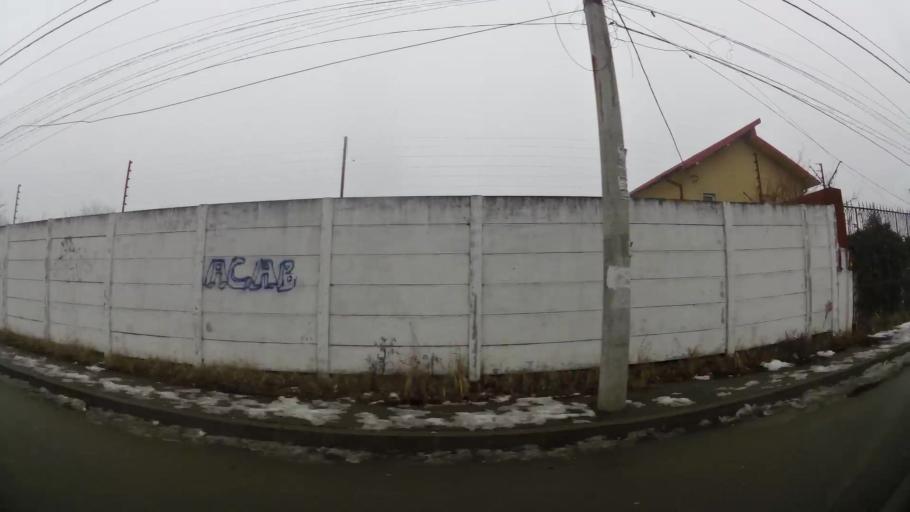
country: RO
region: Ilfov
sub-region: Comuna Chiajna
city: Rosu
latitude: 44.4761
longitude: 26.0052
